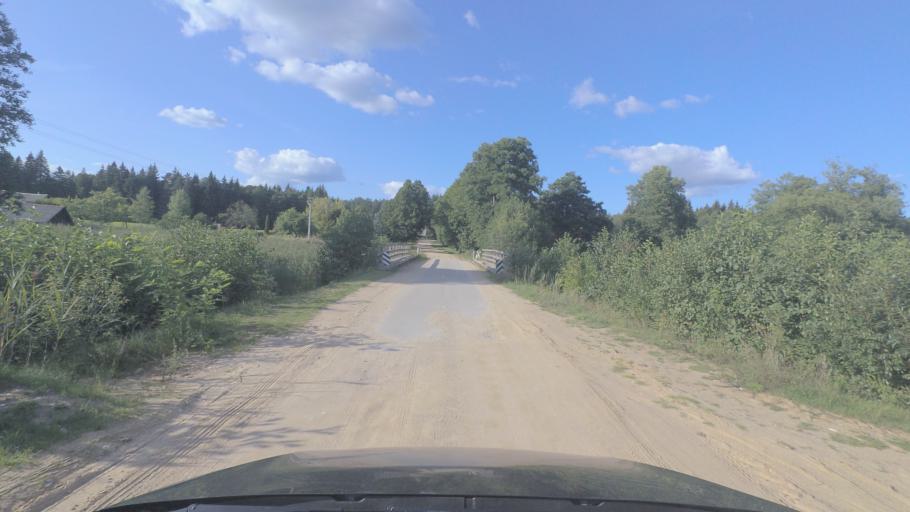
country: LT
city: Pabrade
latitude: 55.1494
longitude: 25.7650
